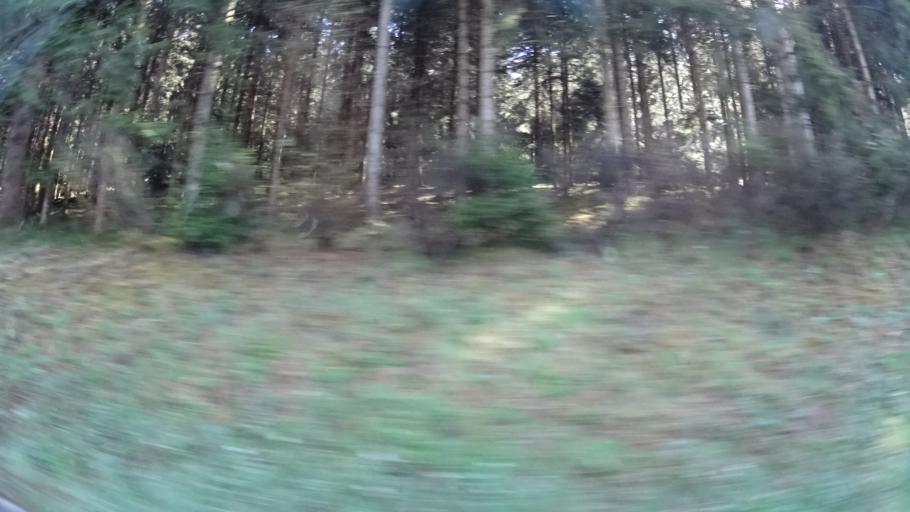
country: DE
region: Baden-Wuerttemberg
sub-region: Karlsruhe Region
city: Bad Wildbad
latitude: 48.7053
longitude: 8.5622
